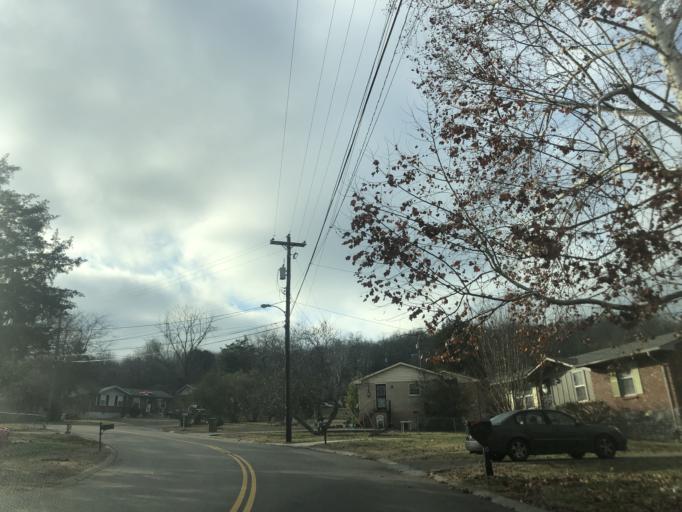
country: US
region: Tennessee
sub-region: Davidson County
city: Nashville
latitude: 36.2196
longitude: -86.7930
